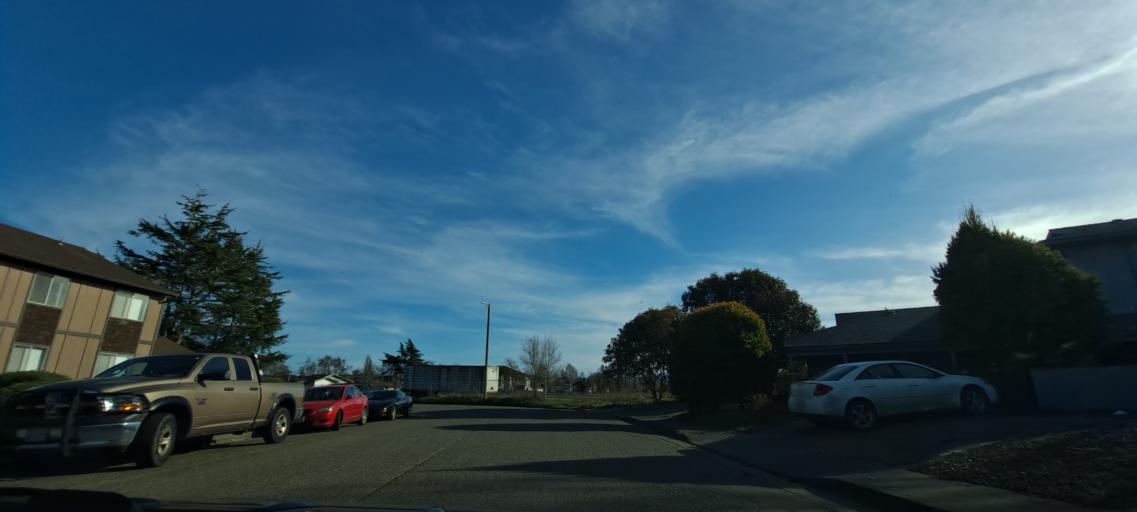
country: US
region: California
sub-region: Humboldt County
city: Fortuna
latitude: 40.5924
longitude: -124.1561
